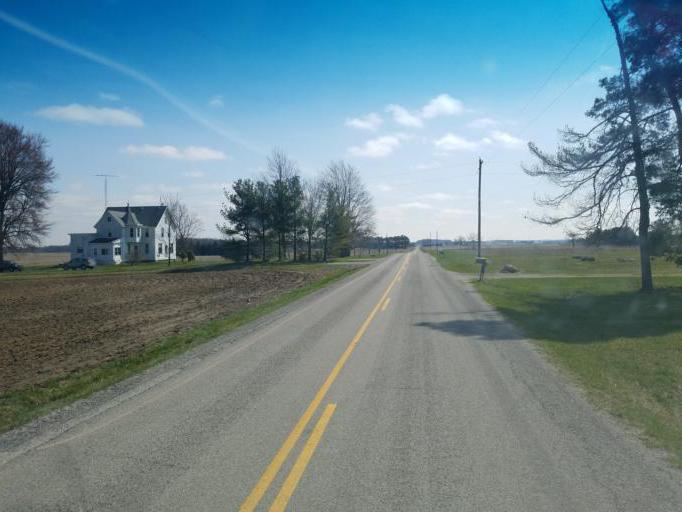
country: US
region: Ohio
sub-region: Crawford County
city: Bucyrus
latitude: 40.8998
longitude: -82.9291
